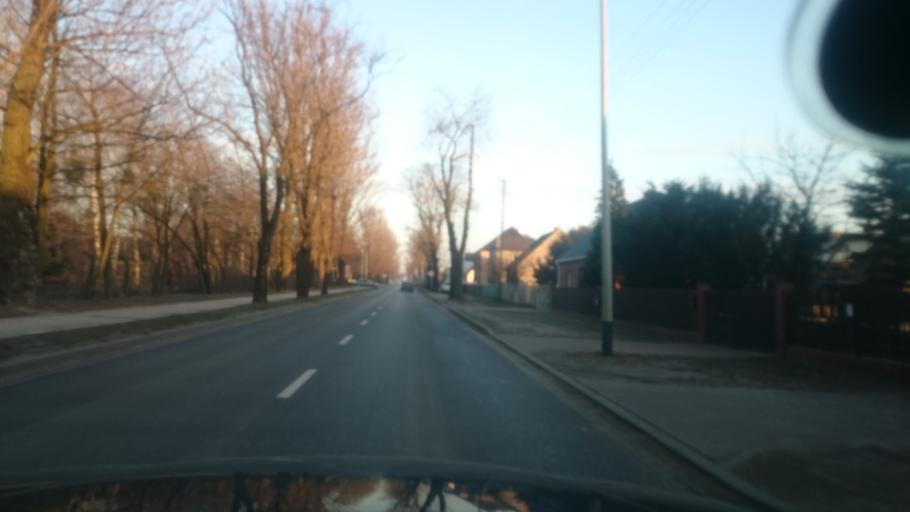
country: PL
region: Greater Poland Voivodeship
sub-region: Powiat ostrowski
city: Ostrow Wielkopolski
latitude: 51.6464
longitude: 17.8540
